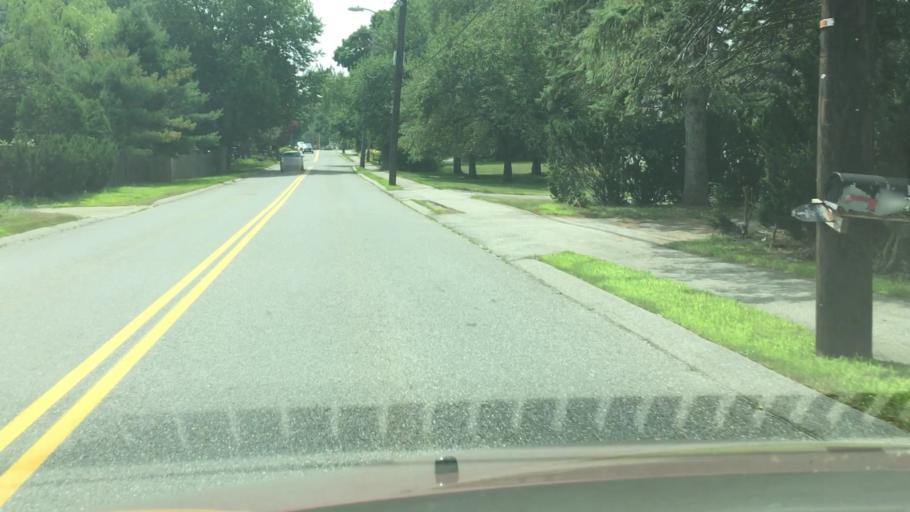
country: US
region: Massachusetts
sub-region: Middlesex County
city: Lexington
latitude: 42.4358
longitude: -71.1896
